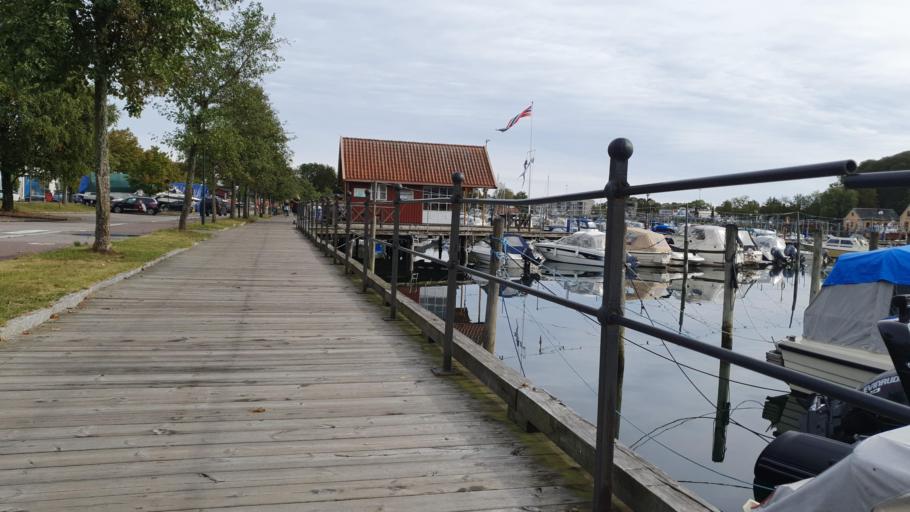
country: NO
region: Vestfold
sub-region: Tonsberg
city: Tonsberg
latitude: 59.2634
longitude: 10.4114
